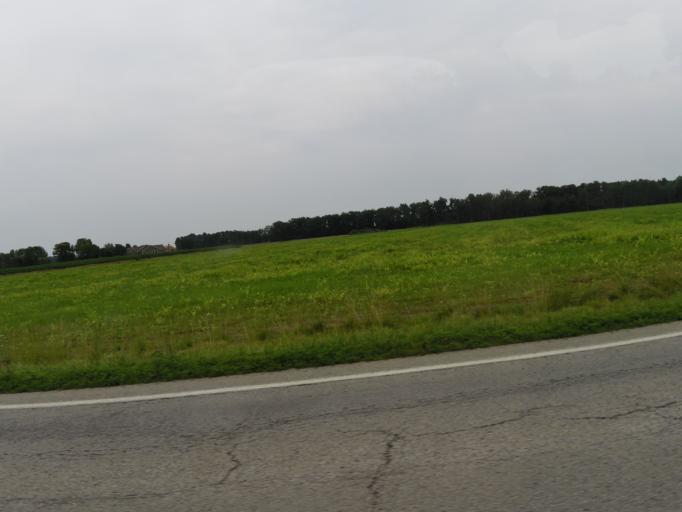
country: US
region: Ohio
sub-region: Brown County
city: Mount Orab
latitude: 39.1360
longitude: -83.9338
